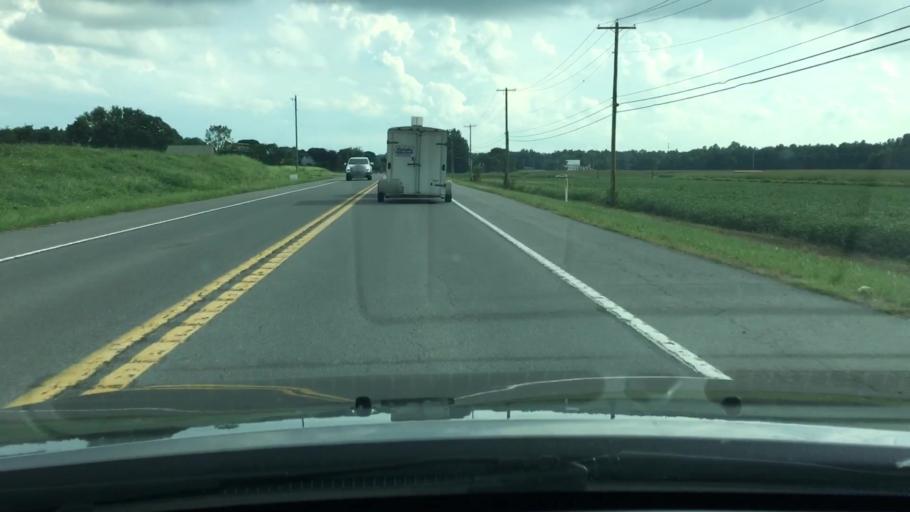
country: US
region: Pennsylvania
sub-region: Franklin County
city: Scotland
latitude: 39.9482
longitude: -77.5839
